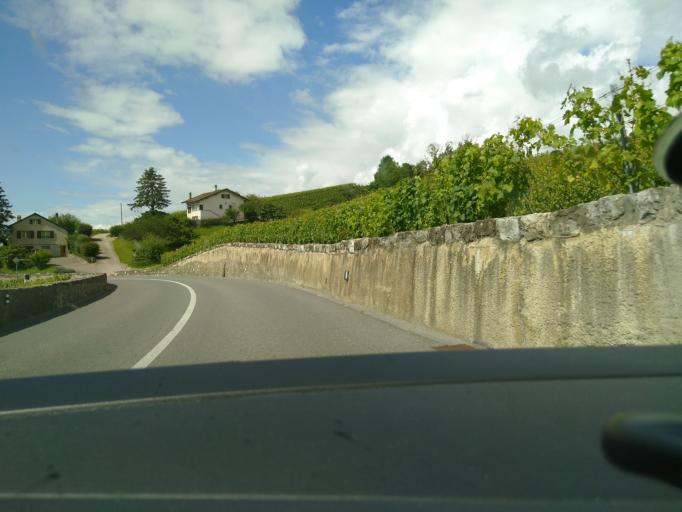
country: CH
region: Vaud
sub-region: Morges District
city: Aubonne
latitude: 46.4850
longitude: 6.3758
